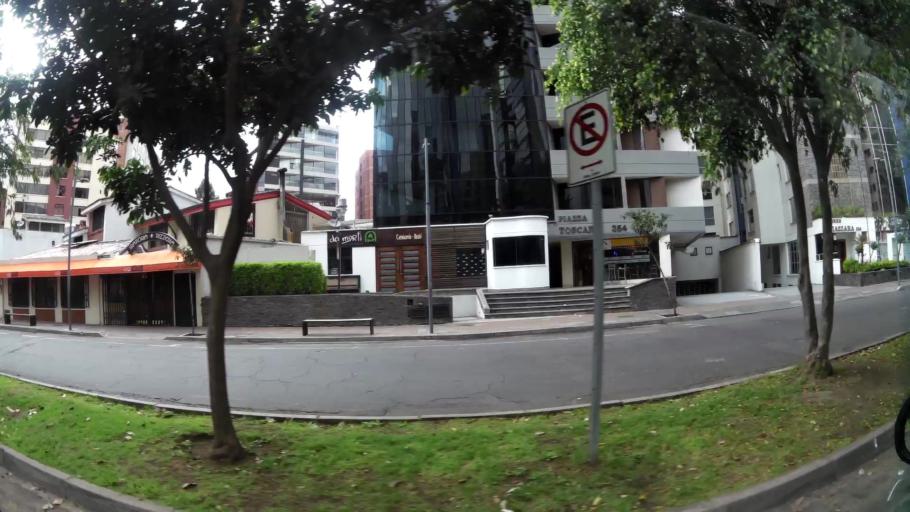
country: EC
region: Pichincha
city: Quito
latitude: -0.1849
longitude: -78.4809
